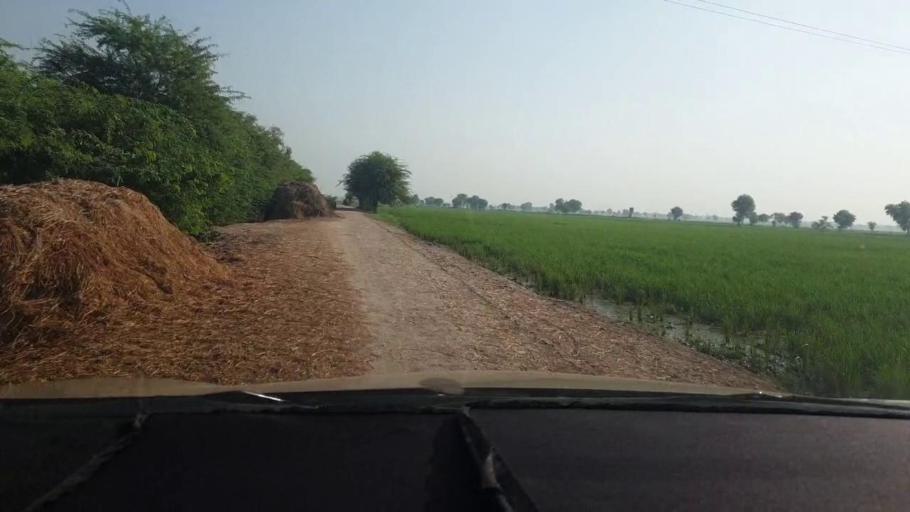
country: PK
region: Sindh
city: Kambar
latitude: 27.5827
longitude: 68.1011
